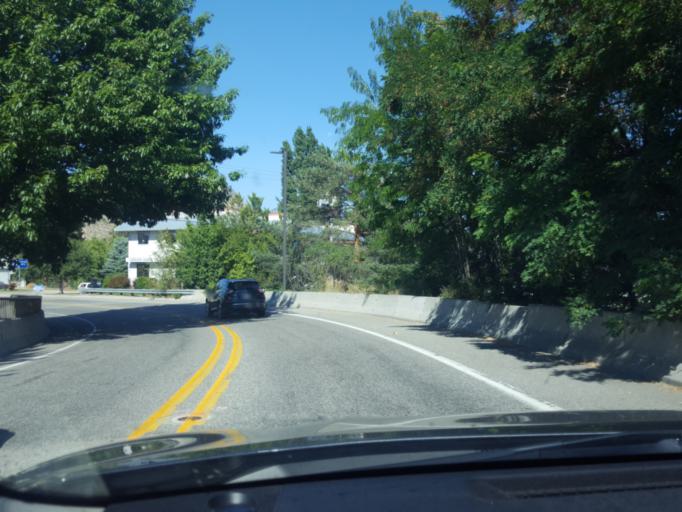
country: US
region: Washington
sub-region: Chelan County
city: Chelan
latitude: 47.8364
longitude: -120.0156
